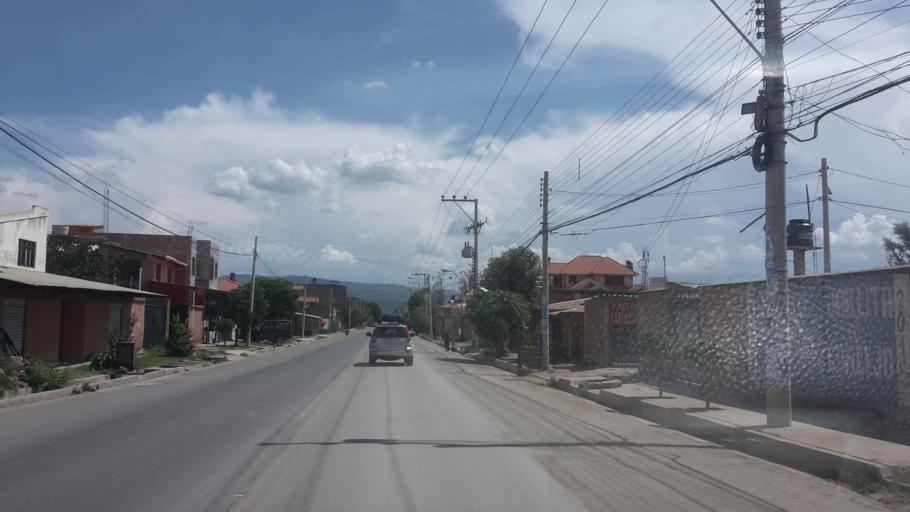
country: BO
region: Cochabamba
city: Cochabamba
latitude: -17.3687
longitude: -66.2314
